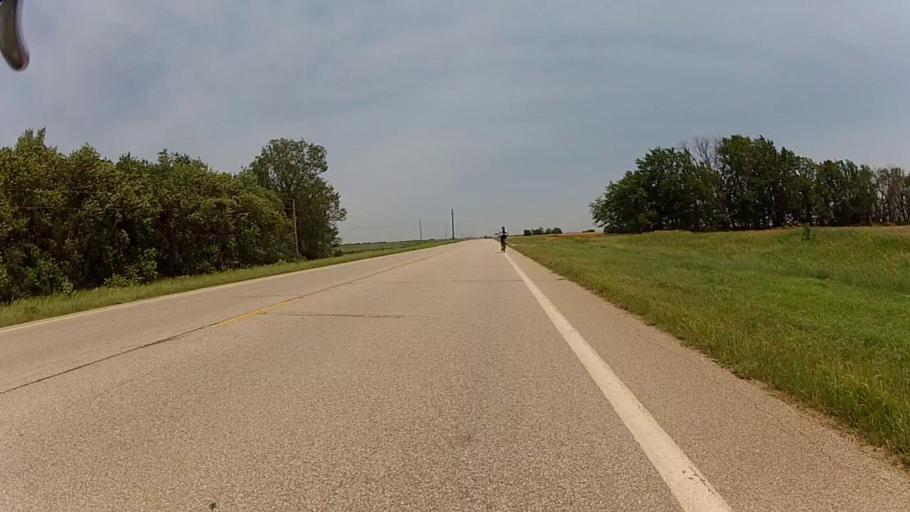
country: US
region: Kansas
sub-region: Cowley County
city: Arkansas City
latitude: 37.0562
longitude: -97.1402
